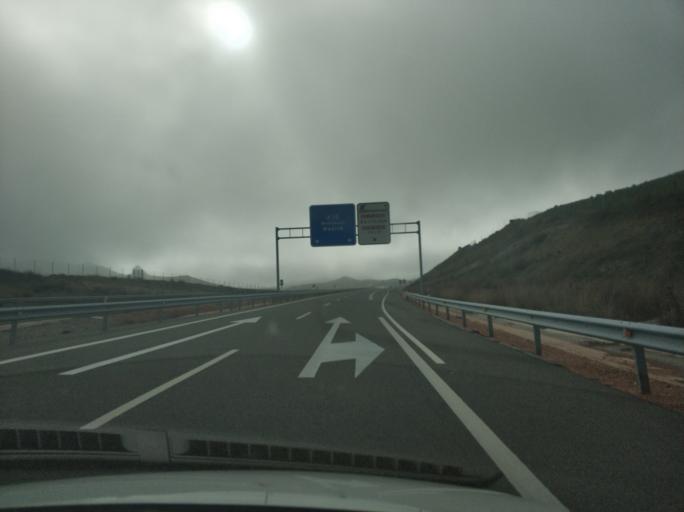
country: ES
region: Castille and Leon
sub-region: Provincia de Soria
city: Yelo
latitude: 41.2234
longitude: -2.4729
